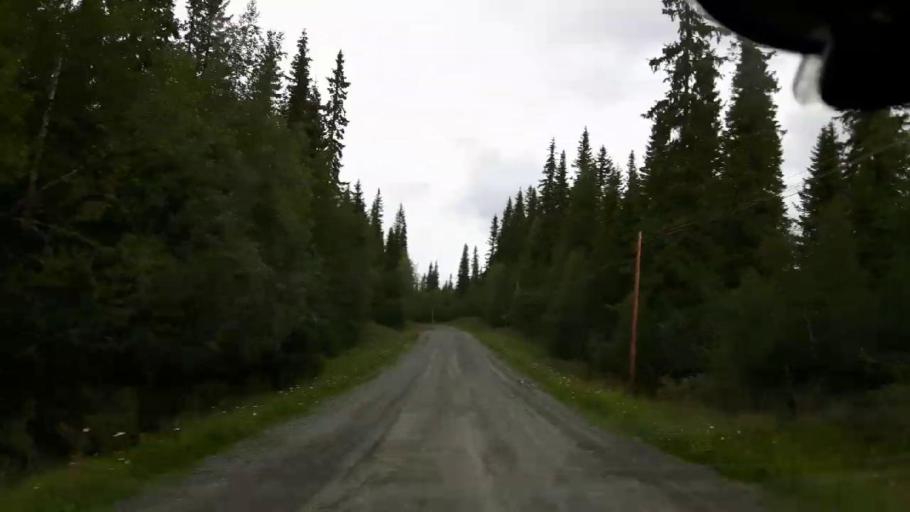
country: SE
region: Jaemtland
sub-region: Krokoms Kommun
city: Valla
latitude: 63.7169
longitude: 13.8590
